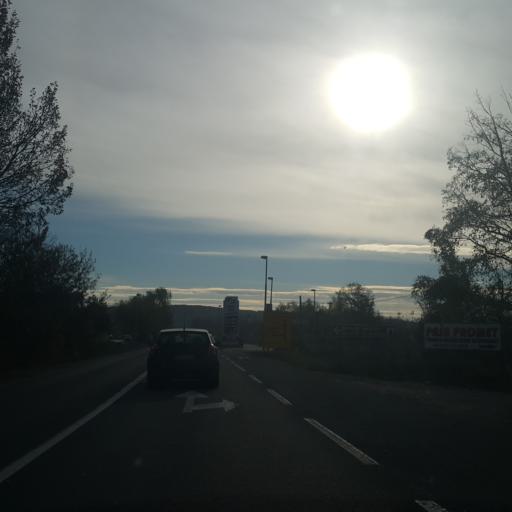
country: RS
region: Central Serbia
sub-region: Belgrade
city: Lazarevac
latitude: 44.3925
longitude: 20.2405
